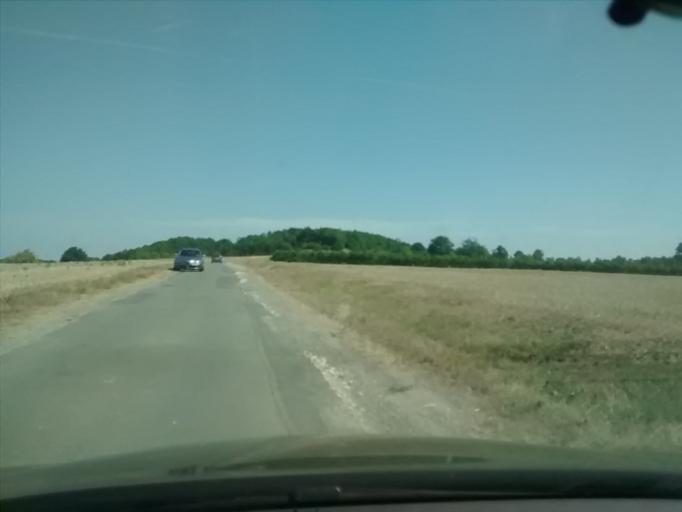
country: FR
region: Aquitaine
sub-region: Departement de la Dordogne
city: Monbazillac
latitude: 44.7639
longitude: 0.4706
